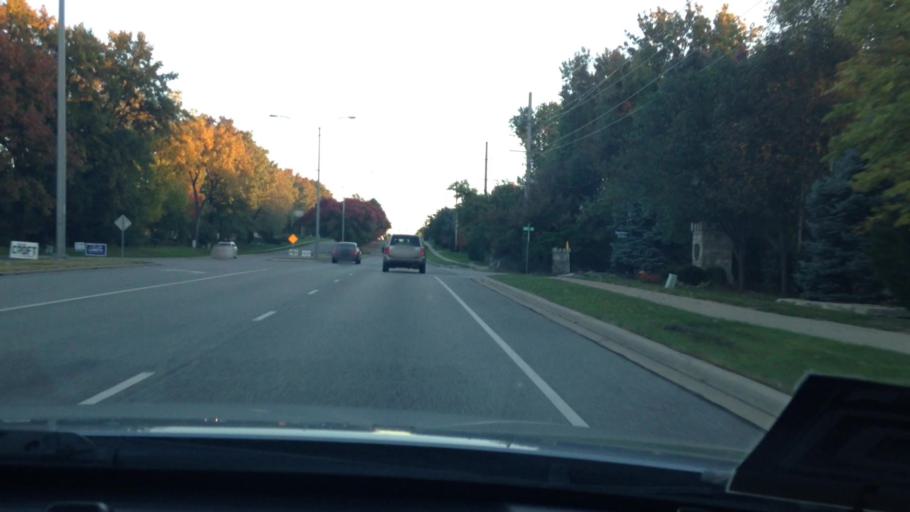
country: US
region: Kansas
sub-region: Johnson County
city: Lenexa
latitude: 38.9103
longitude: -94.7053
